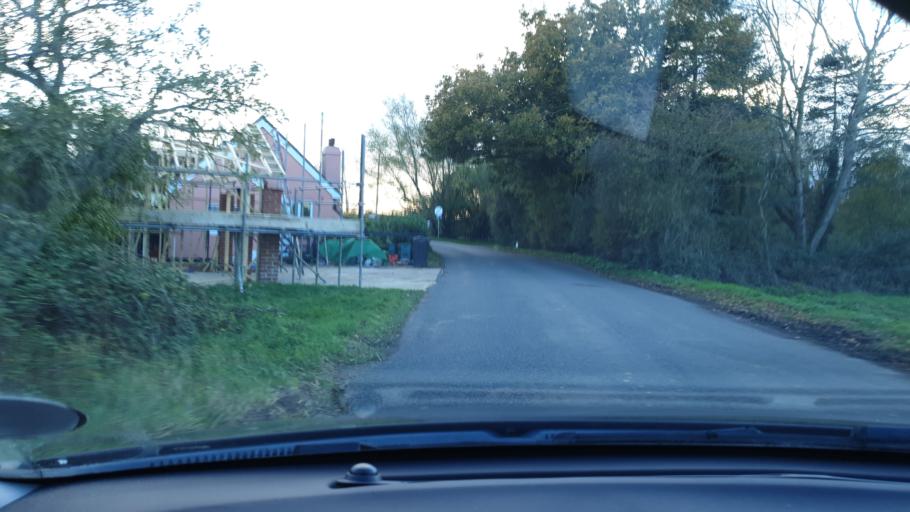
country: GB
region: England
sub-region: Essex
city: Mistley
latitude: 51.8997
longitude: 1.1411
